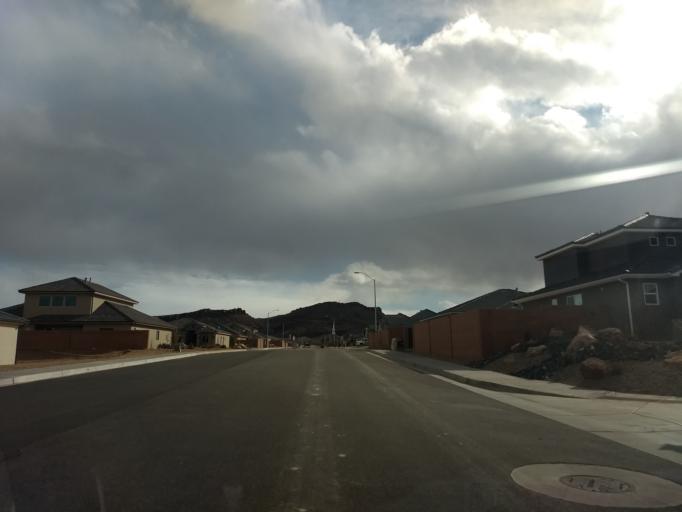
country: US
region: Utah
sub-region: Washington County
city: Washington
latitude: 37.0563
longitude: -113.5176
